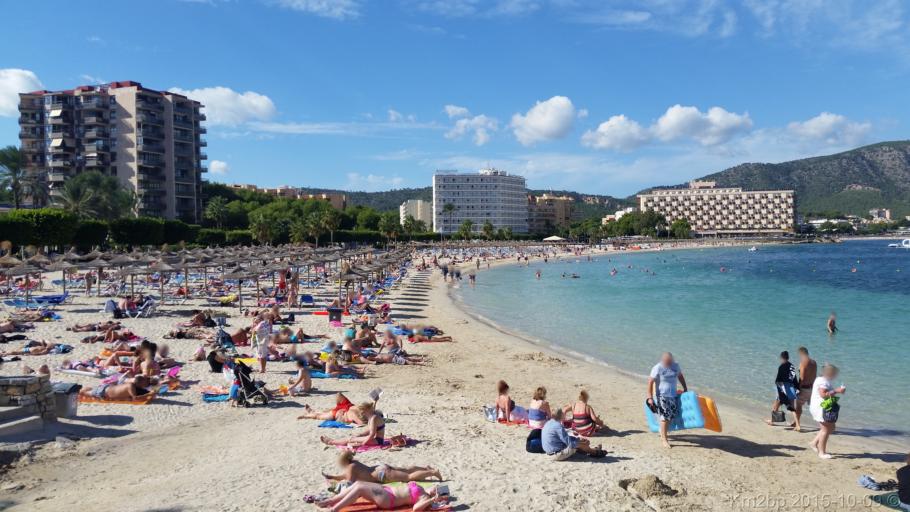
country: ES
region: Balearic Islands
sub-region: Illes Balears
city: Magaluf
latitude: 39.5124
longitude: 2.5399
